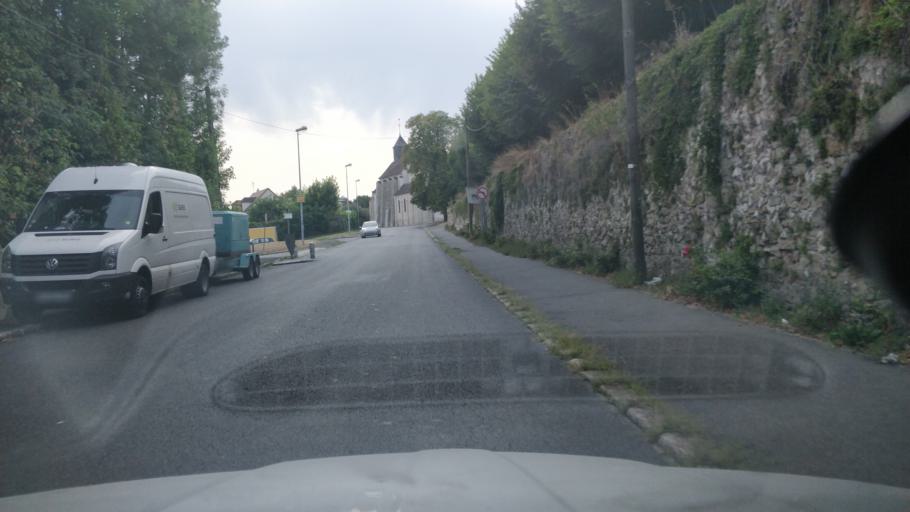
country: FR
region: Ile-de-France
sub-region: Departement de Seine-et-Marne
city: Pomponne
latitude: 48.8811
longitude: 2.6845
